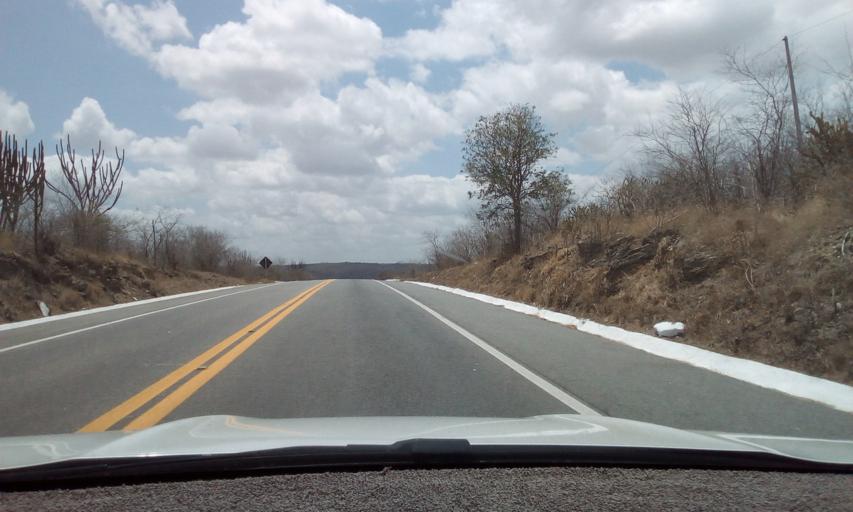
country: BR
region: Paraiba
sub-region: Boqueirao
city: Boqueirao
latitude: -7.6730
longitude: -36.0785
